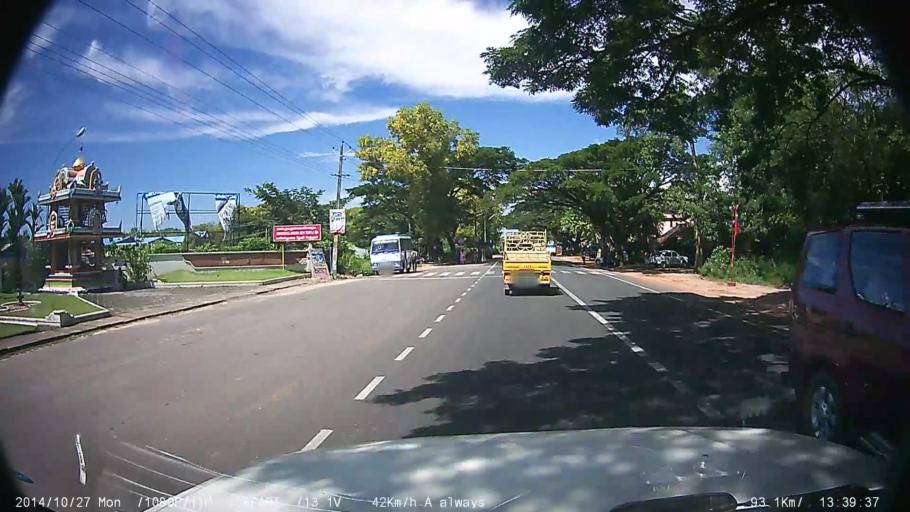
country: IN
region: Kerala
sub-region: Alappuzha
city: Shertallai
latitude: 9.6279
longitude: 76.3329
